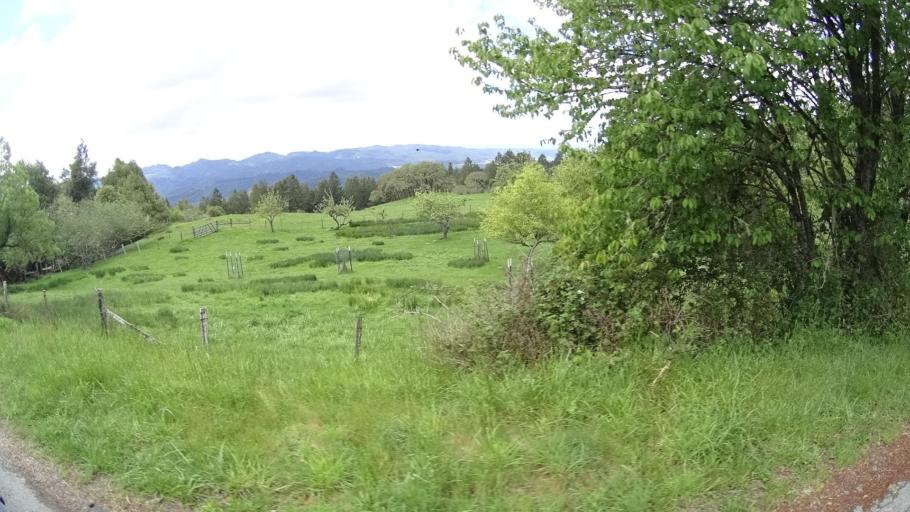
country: US
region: California
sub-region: Humboldt County
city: Blue Lake
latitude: 40.8551
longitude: -123.9242
